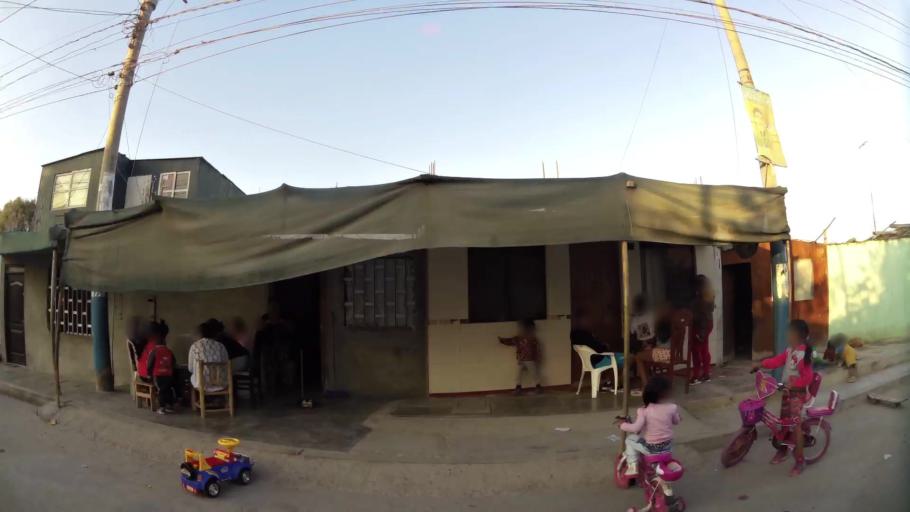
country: PE
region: Ica
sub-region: Provincia de Pisco
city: Villa Tupac Amaru
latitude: -13.7020
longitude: -76.1519
